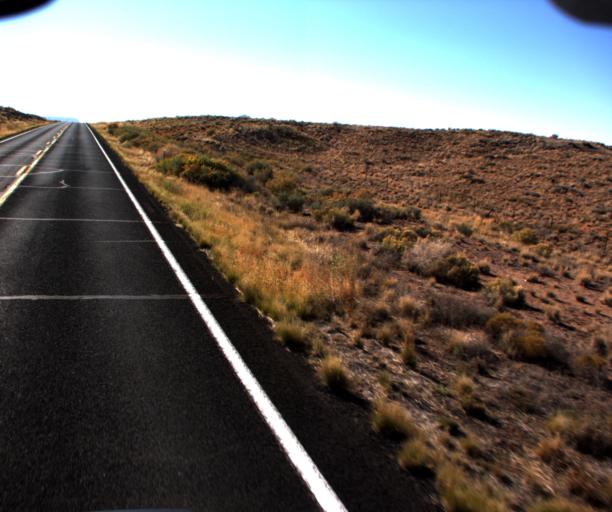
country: US
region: Arizona
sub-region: Navajo County
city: Dilkon
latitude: 35.5550
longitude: -110.4544
